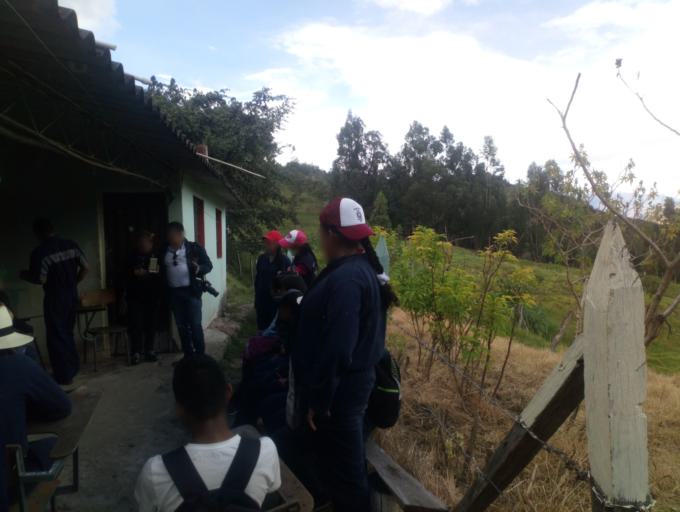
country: CO
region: Boyaca
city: Socota
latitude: 6.0964
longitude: -72.7178
